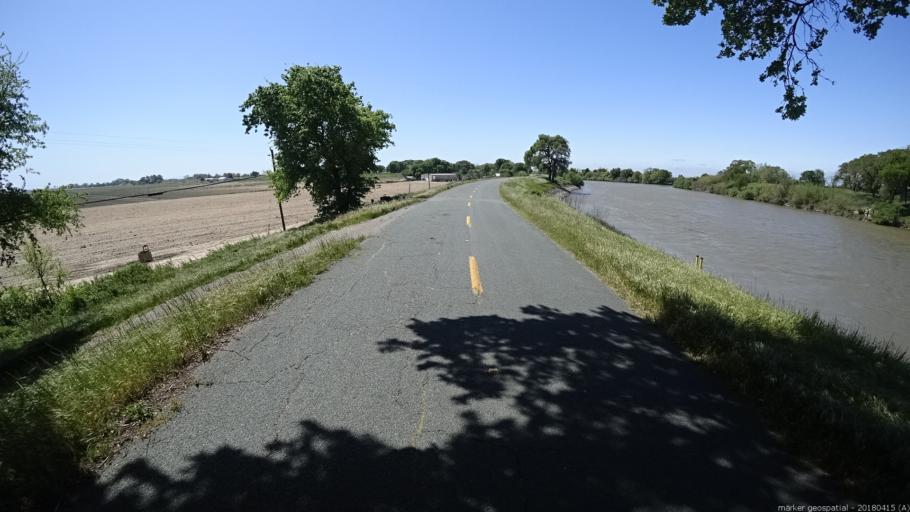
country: US
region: California
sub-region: Sacramento County
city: Walnut Grove
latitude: 38.2544
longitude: -121.5968
